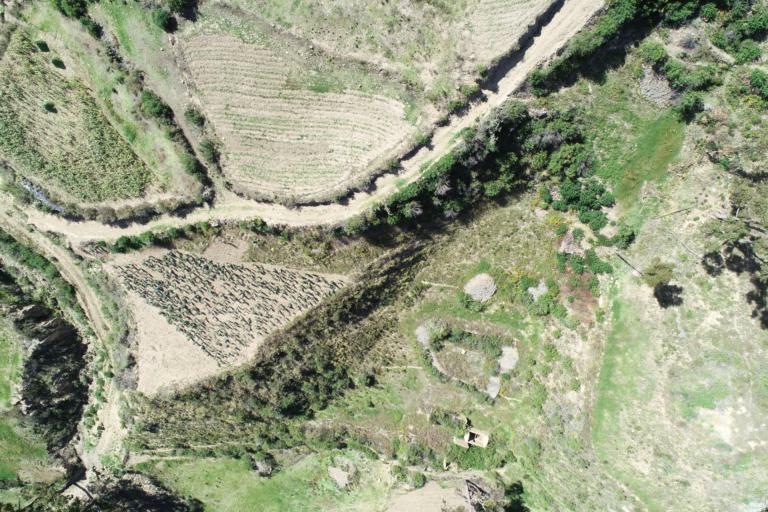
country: BO
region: La Paz
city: La Paz
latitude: -16.5525
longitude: -67.9871
